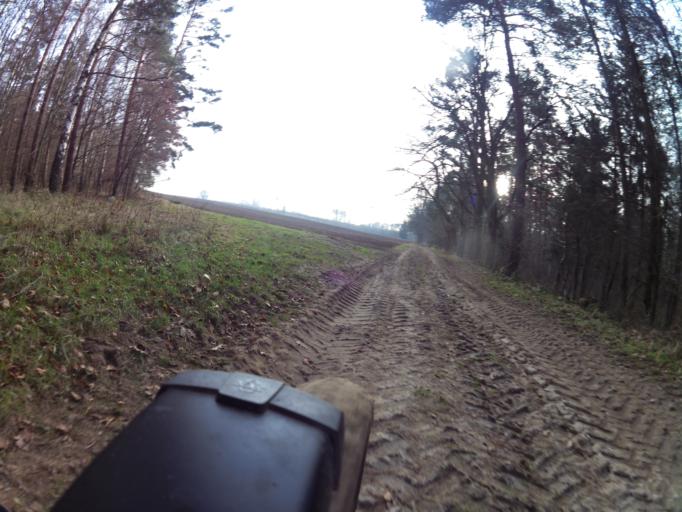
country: PL
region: West Pomeranian Voivodeship
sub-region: Powiat koszalinski
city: Polanow
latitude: 54.1466
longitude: 16.7302
